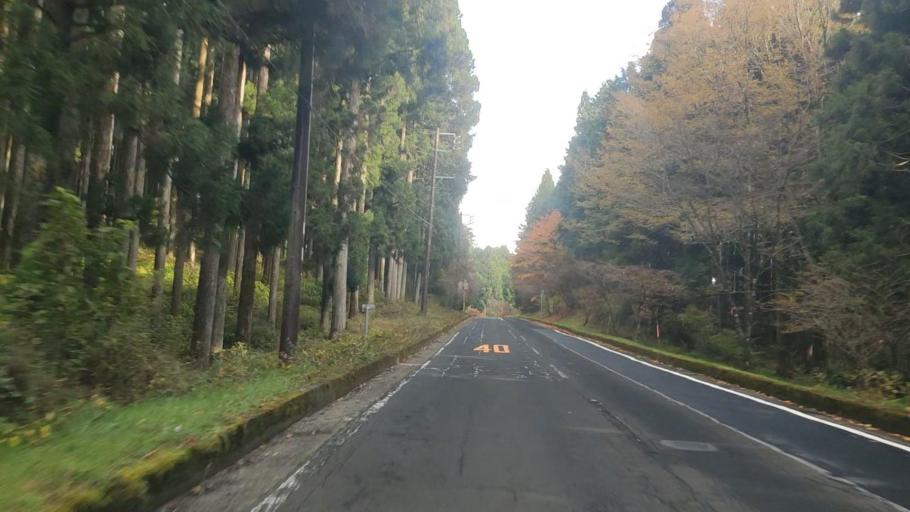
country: JP
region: Shizuoka
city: Fujinomiya
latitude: 35.3042
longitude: 138.6760
